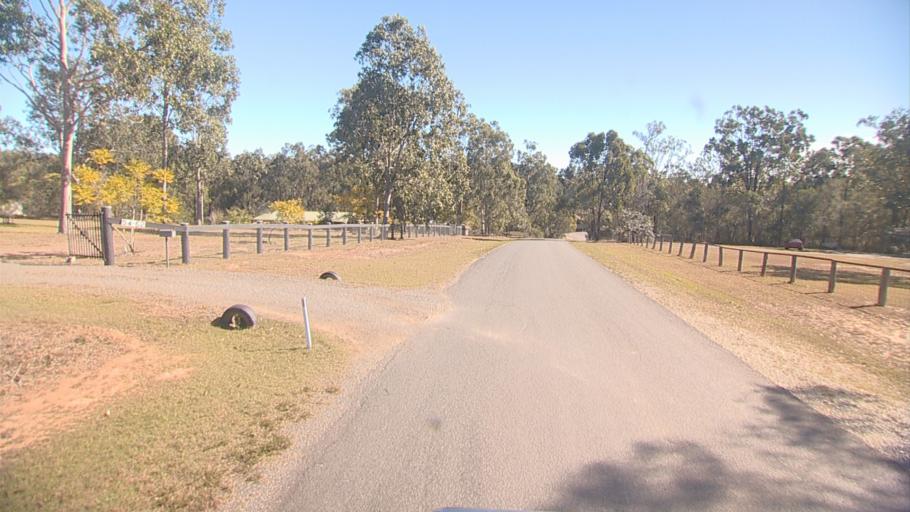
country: AU
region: Queensland
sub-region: Ipswich
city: Springfield Lakes
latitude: -27.7190
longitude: 152.9252
